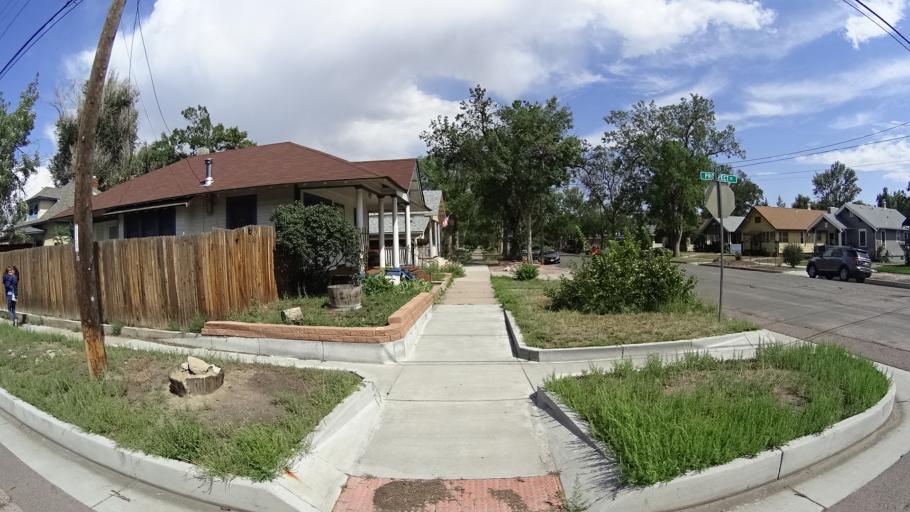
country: US
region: Colorado
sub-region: El Paso County
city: Colorado Springs
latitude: 38.8406
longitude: -104.8103
